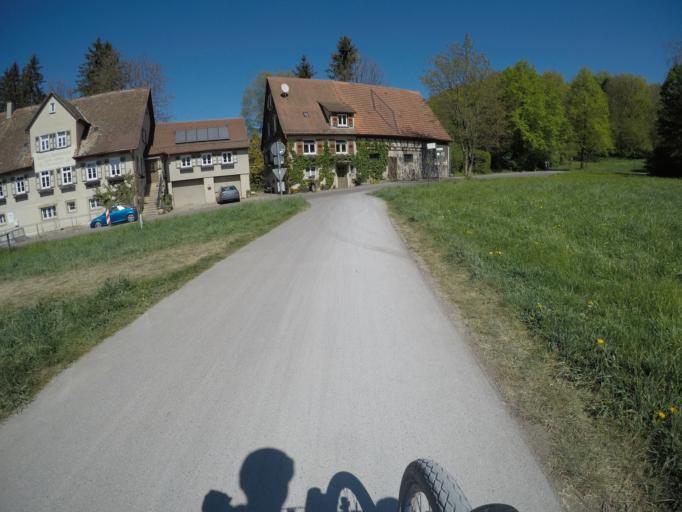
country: DE
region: Baden-Wuerttemberg
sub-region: Regierungsbezirk Stuttgart
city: Waiblingen
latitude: 48.8625
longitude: 9.3040
